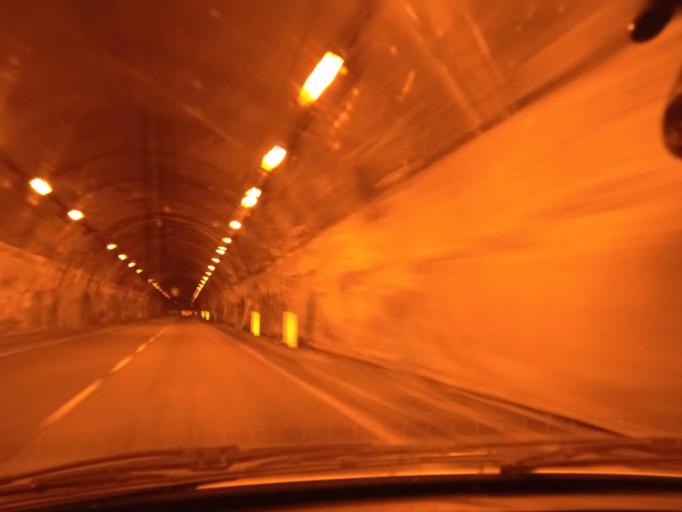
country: IT
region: Sicily
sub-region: Messina
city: Brolo
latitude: 38.1529
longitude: 14.8373
